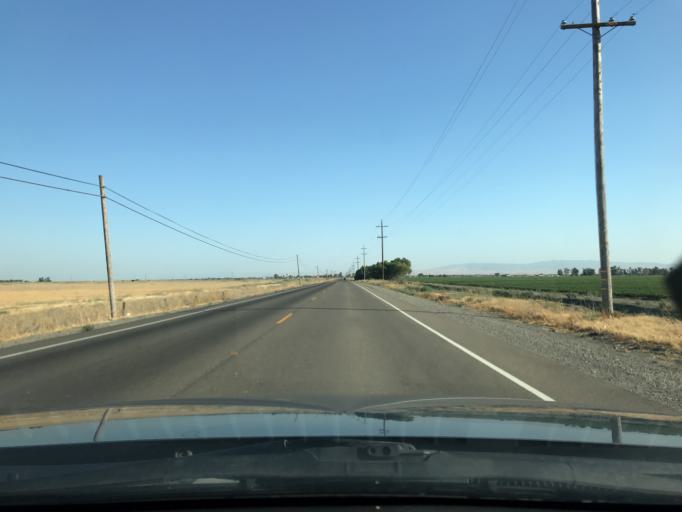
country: US
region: California
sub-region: Merced County
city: Los Banos
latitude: 37.1212
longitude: -120.8349
